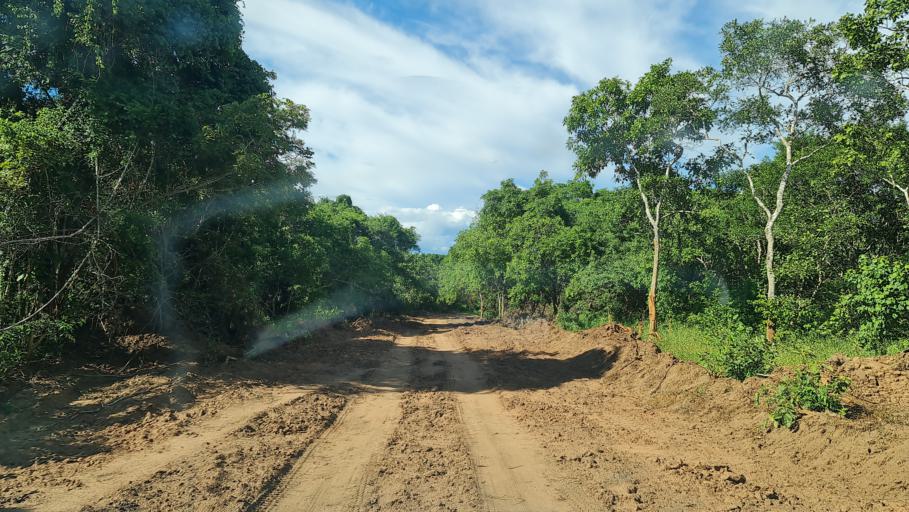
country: MZ
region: Nampula
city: Antonio Enes
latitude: -15.5132
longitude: 40.1313
